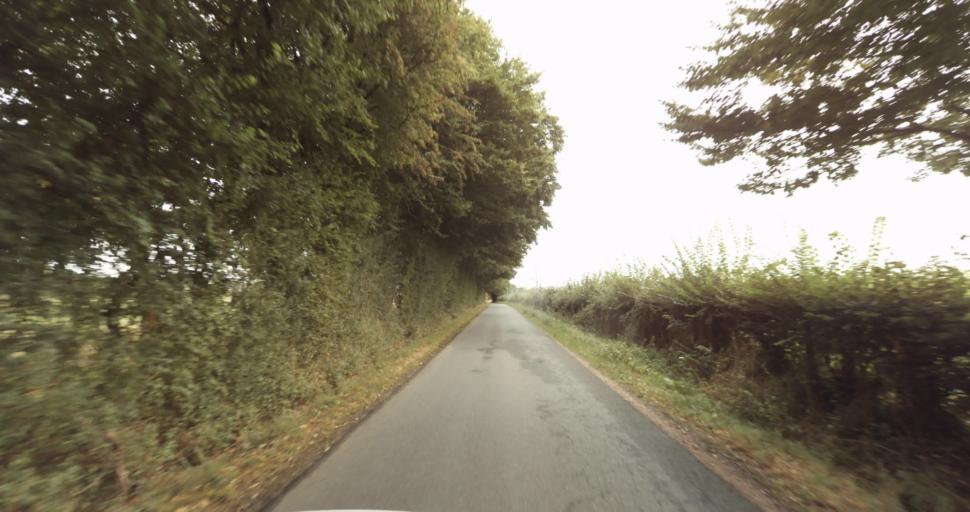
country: FR
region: Lower Normandy
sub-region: Departement du Calvados
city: Livarot
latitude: 48.9411
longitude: 0.1137
